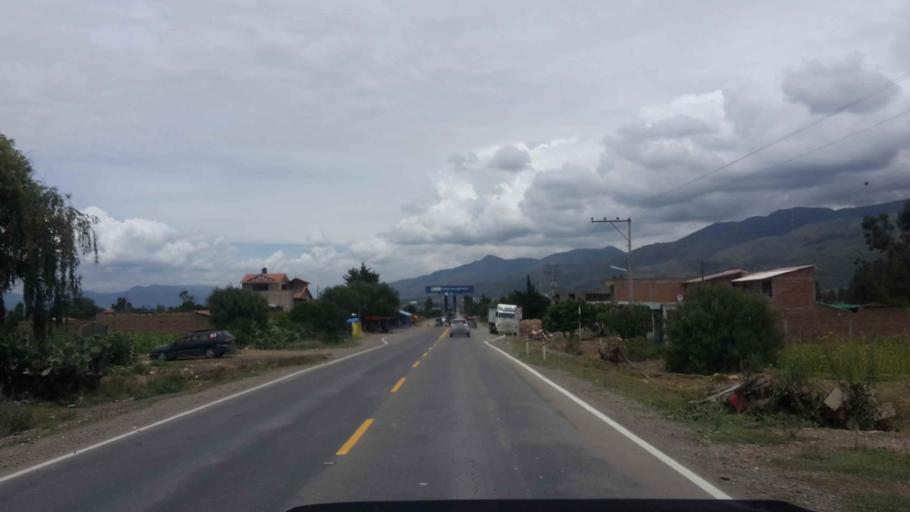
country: BO
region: Cochabamba
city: Punata
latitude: -17.5149
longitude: -65.8248
